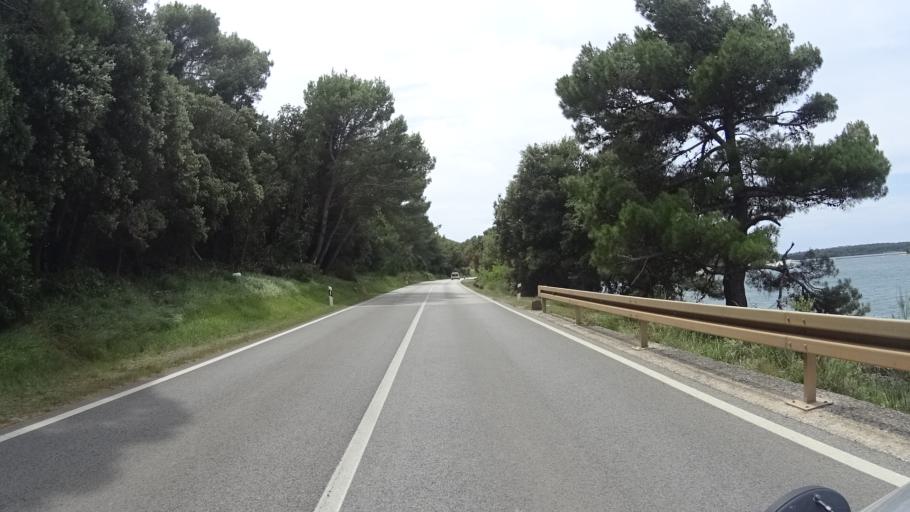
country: HR
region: Istarska
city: Medulin
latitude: 44.8150
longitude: 13.9063
